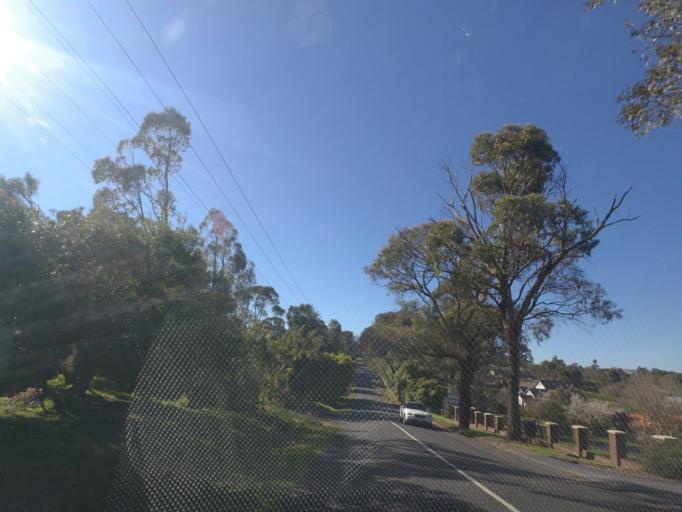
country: AU
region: Victoria
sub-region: Maroondah
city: Croydon Hills
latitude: -37.7409
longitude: 145.2693
